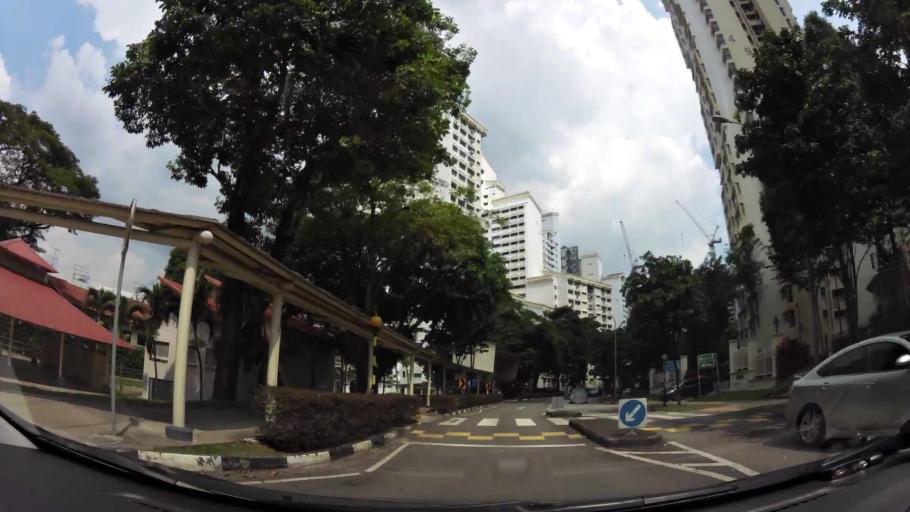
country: SG
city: Singapore
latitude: 1.2943
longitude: 103.8076
